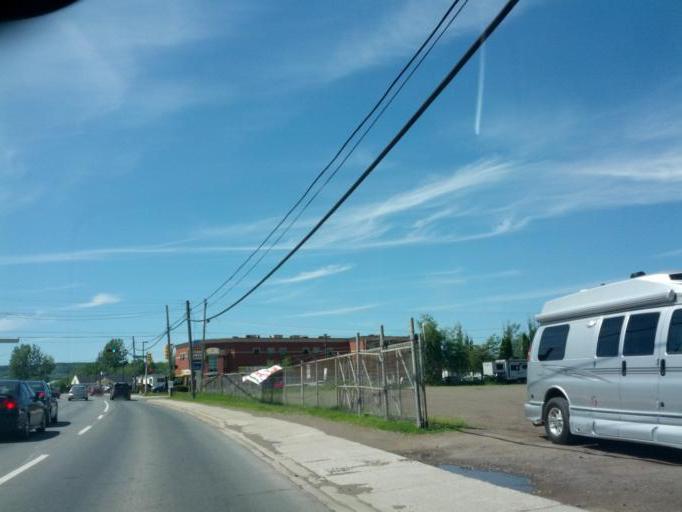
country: CA
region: New Brunswick
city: Moncton
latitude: 46.1205
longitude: -64.8448
